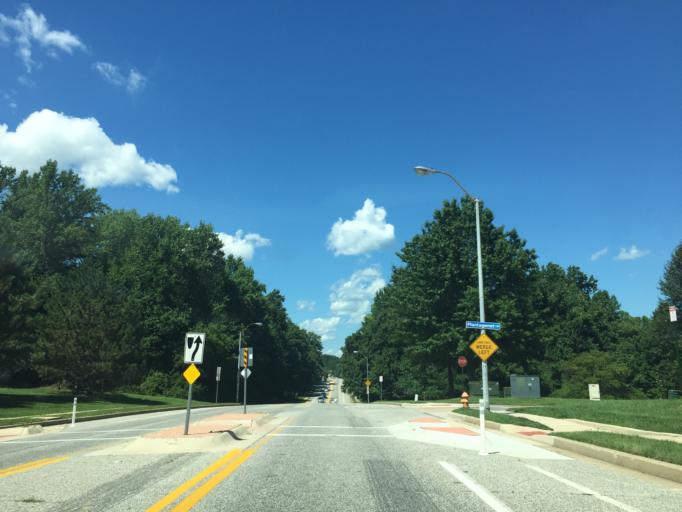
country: US
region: Maryland
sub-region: Baltimore County
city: Perry Hall
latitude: 39.4042
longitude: -76.4860
